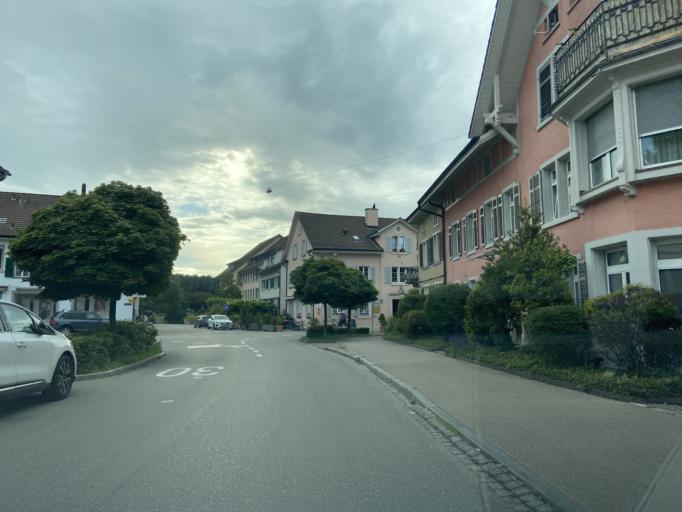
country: CH
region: Zurich
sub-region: Bezirk Winterthur
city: Elgg / Staedtchen und Umgebung
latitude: 47.4910
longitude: 8.8671
